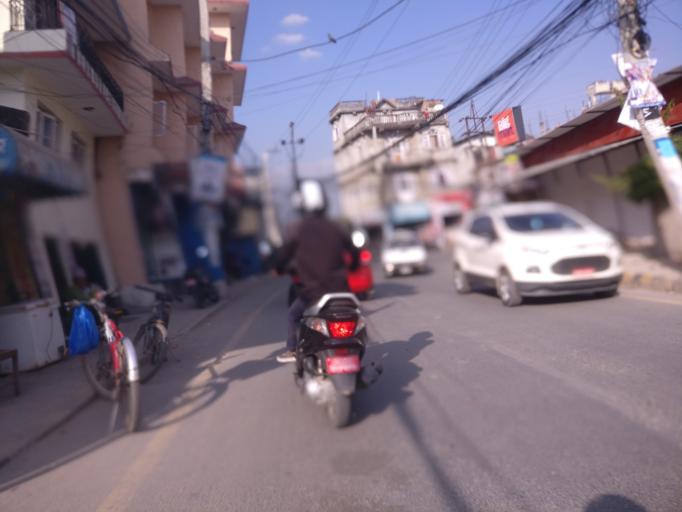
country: NP
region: Central Region
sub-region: Bagmati Zone
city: Patan
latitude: 27.6869
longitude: 85.3137
